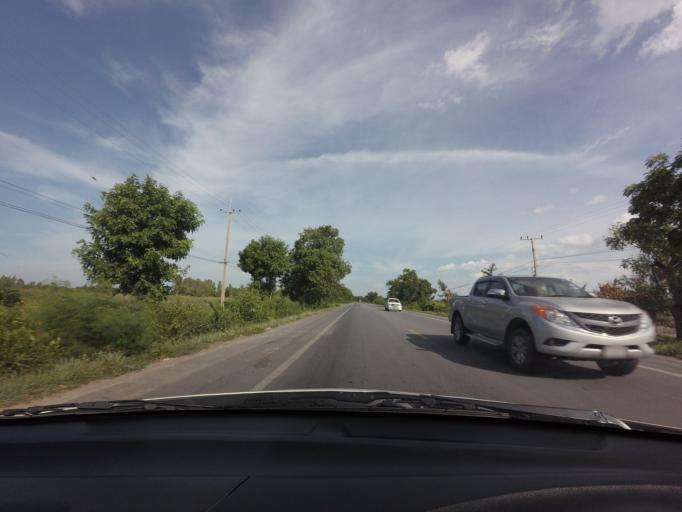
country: TH
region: Kanchanaburi
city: Lao Khwan
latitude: 14.5425
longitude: 99.9058
